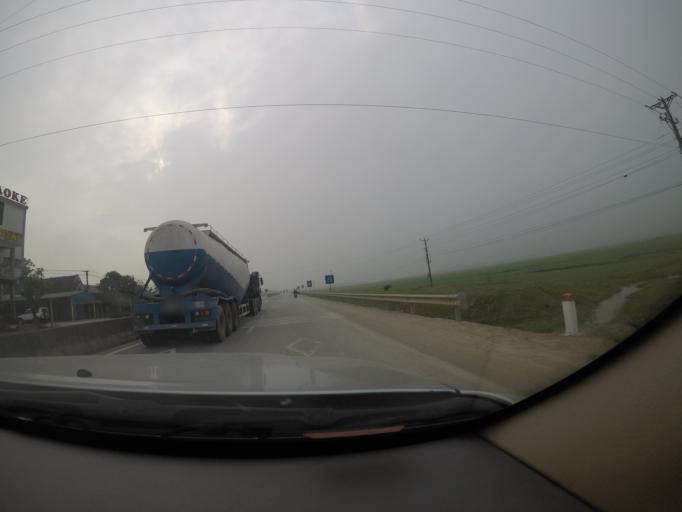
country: VN
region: Ha Tinh
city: Ky Anh
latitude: 18.1881
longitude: 106.1890
